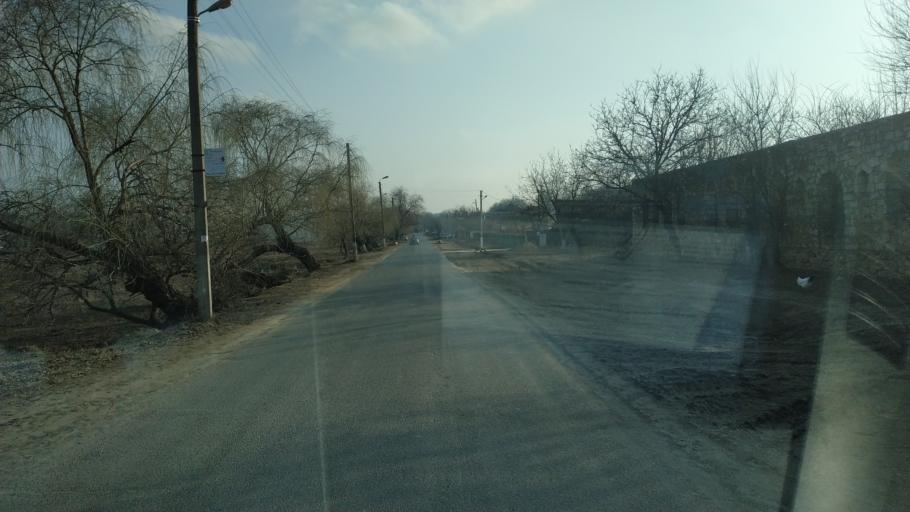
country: MD
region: Hincesti
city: Dancu
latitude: 46.7751
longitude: 28.3461
